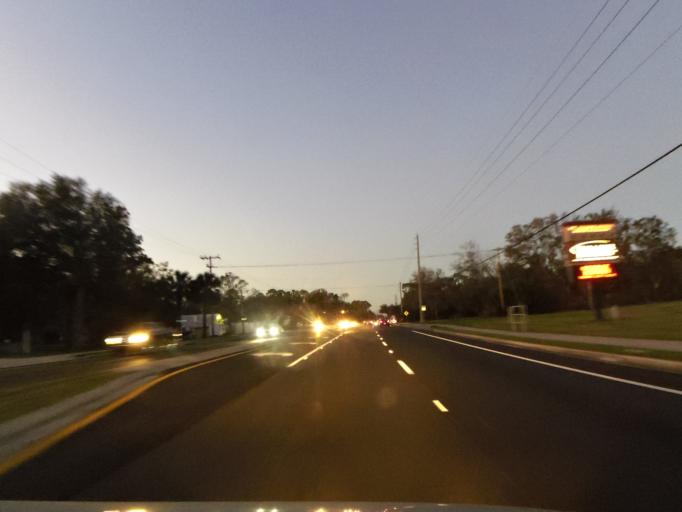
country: US
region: Florida
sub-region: Clay County
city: Lakeside
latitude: 30.1181
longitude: -81.7765
